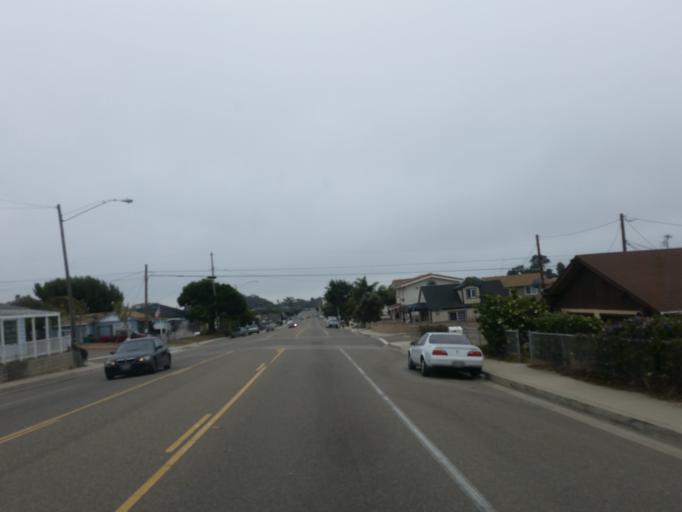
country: US
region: California
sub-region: San Luis Obispo County
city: Grover Beach
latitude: 35.1261
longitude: -120.6262
